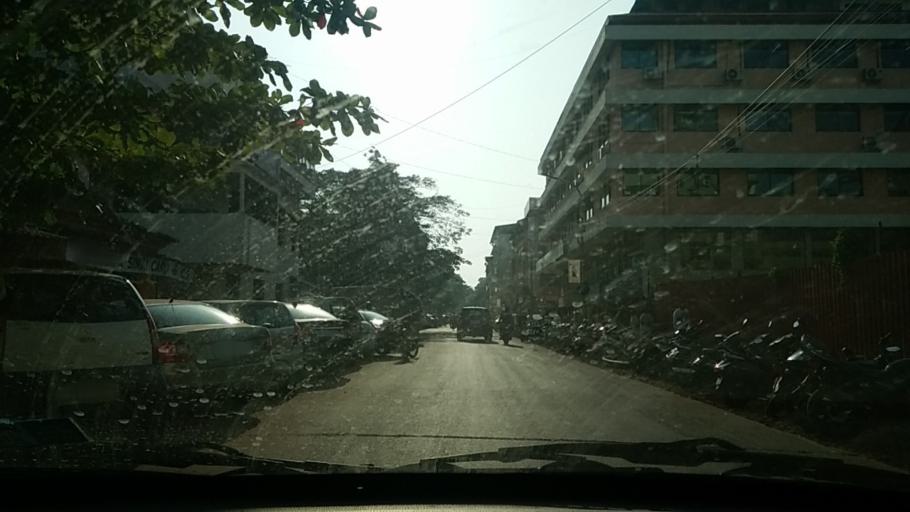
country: IN
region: Goa
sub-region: North Goa
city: Panaji
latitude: 15.4974
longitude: 73.8268
